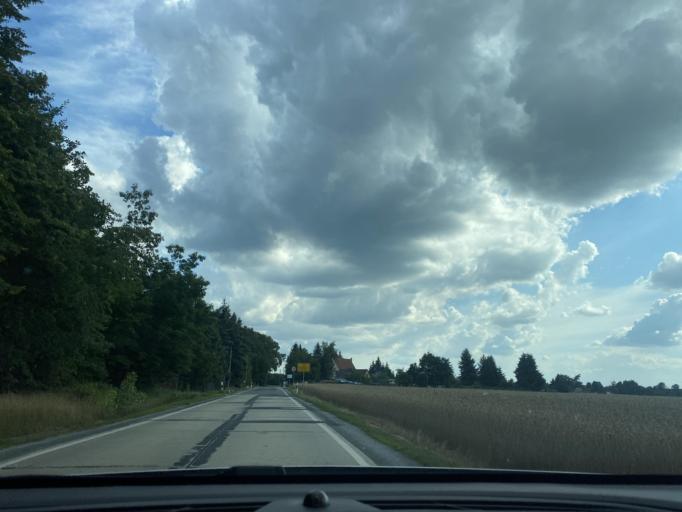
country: DE
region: Saxony
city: Klitten
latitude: 51.3555
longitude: 14.6074
